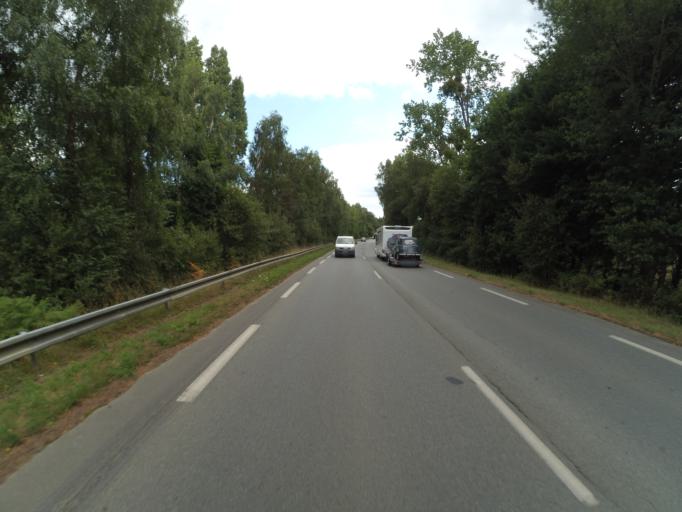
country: FR
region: Brittany
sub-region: Departement du Morbihan
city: Merlevenez
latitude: 47.7503
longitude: -3.2283
